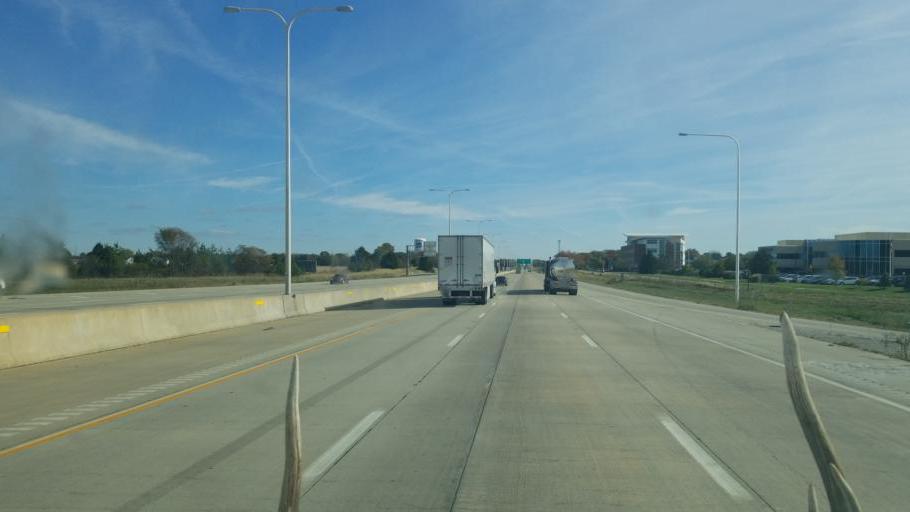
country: US
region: Illinois
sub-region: Effingham County
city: Effingham
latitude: 39.1458
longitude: -88.5286
